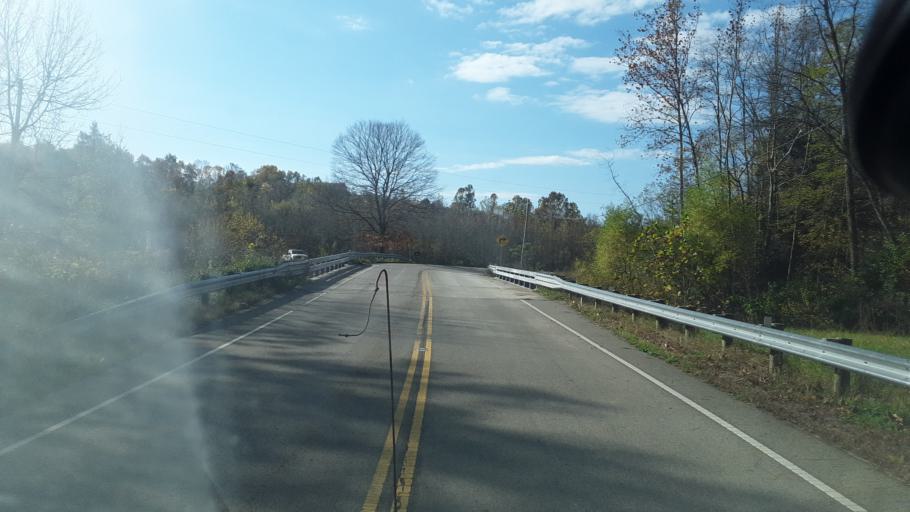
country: US
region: Ohio
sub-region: Highland County
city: Leesburg
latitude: 39.3072
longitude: -83.5163
